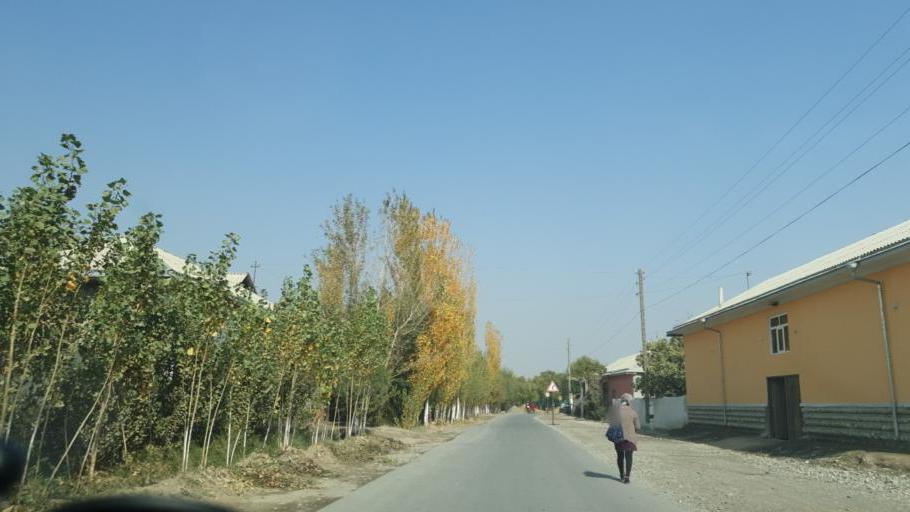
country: UZ
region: Fergana
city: Beshariq
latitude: 40.4936
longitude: 70.6213
